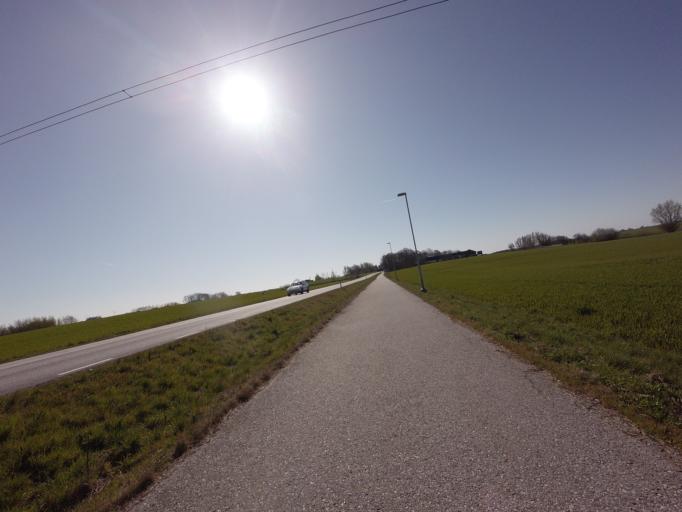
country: SE
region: Skane
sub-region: Malmo
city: Oxie
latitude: 55.4868
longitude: 13.1227
